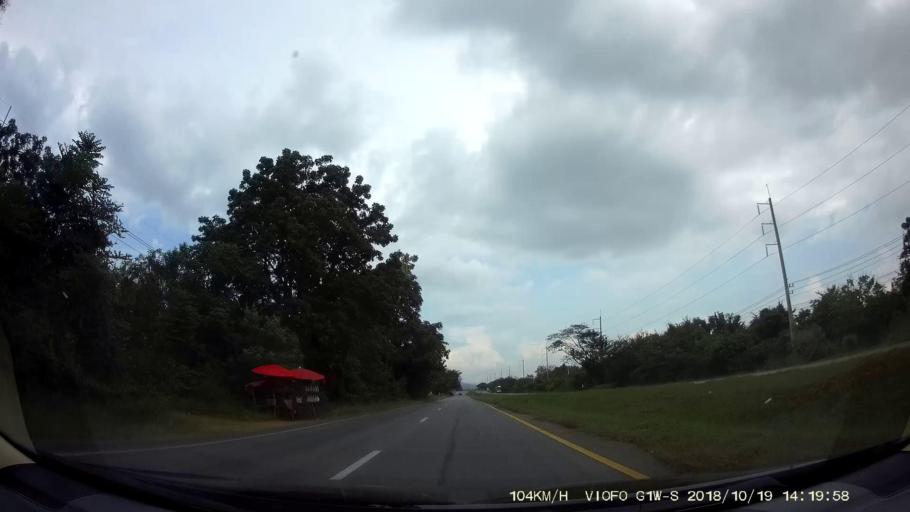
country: TH
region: Chaiyaphum
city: Kaeng Khro
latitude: 16.0347
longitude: 102.2511
